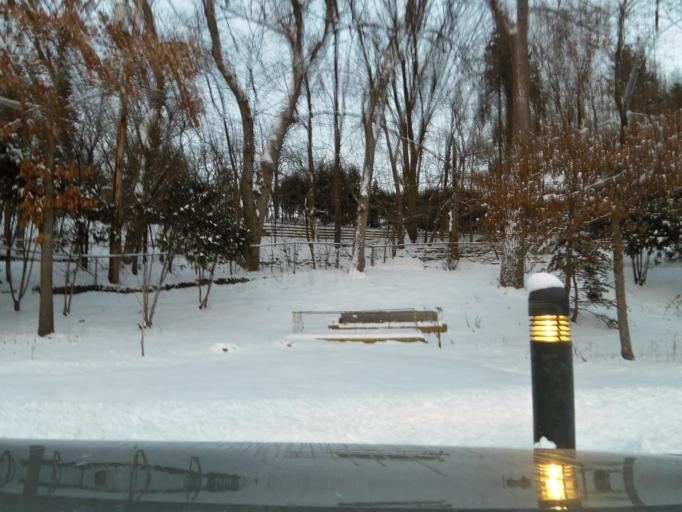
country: US
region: Minnesota
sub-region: Hennepin County
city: Saint Louis Park
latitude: 44.9388
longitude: -93.3212
